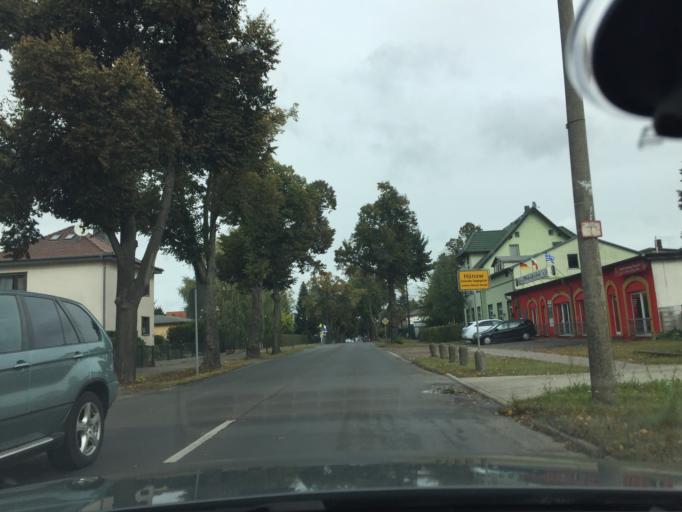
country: DE
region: Berlin
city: Hellersdorf
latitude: 52.5301
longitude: 13.6269
